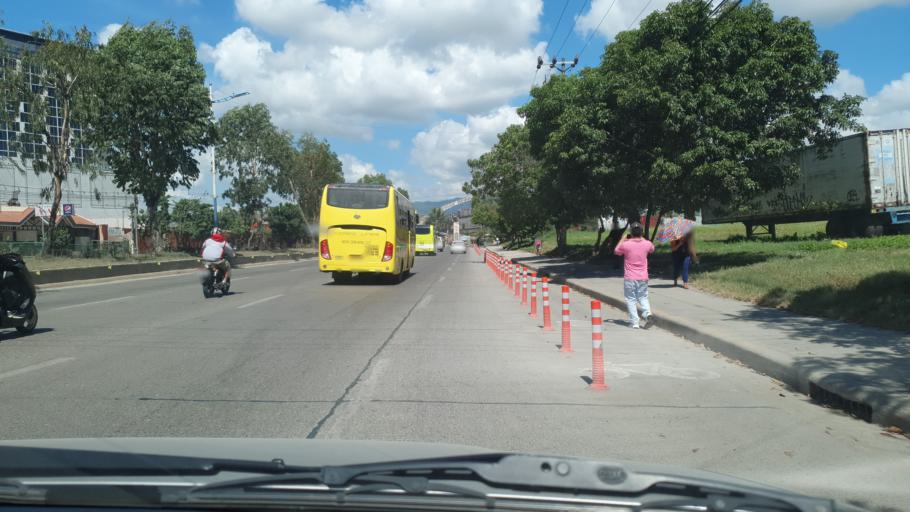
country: PH
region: Central Visayas
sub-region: Lapu-Lapu City
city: Buagsong
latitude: 10.3255
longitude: 123.9394
